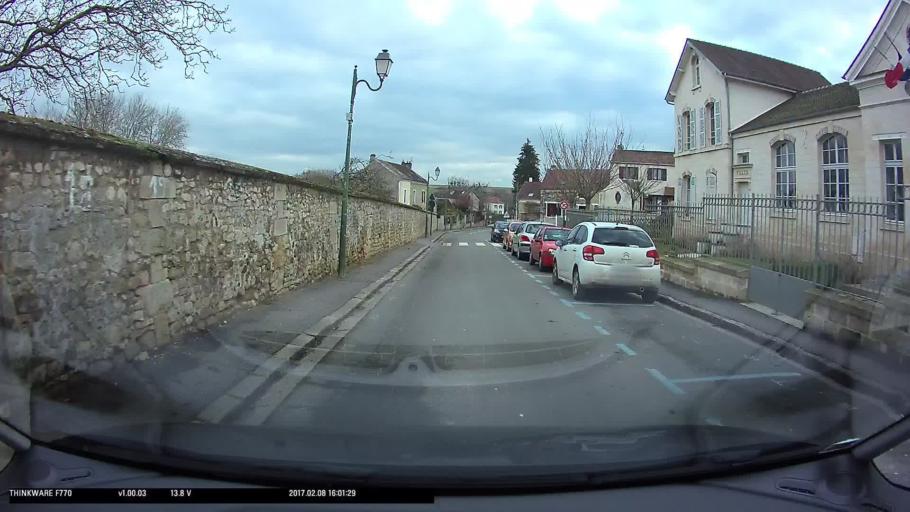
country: FR
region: Ile-de-France
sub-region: Departement du Val-d'Oise
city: Us
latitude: 49.1012
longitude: 1.9673
